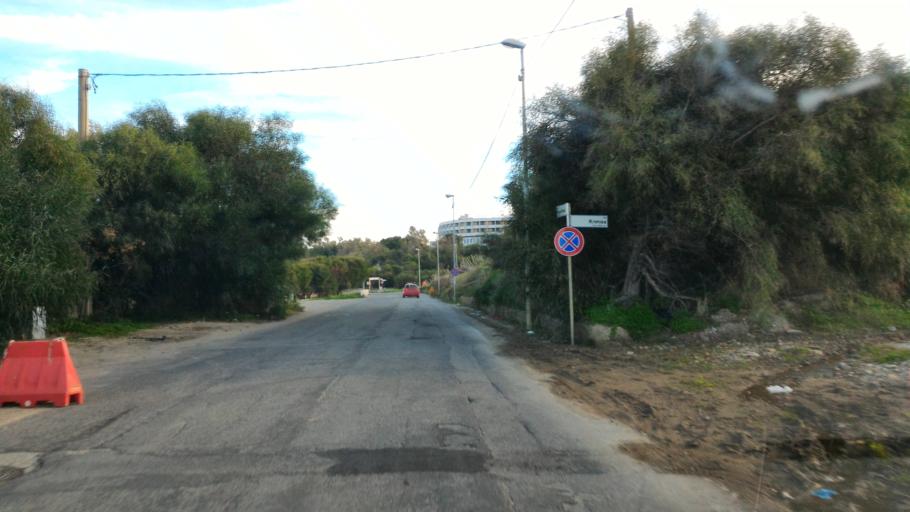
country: IT
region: Calabria
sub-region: Provincia di Crotone
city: Crotone
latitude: 39.0525
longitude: 17.1394
